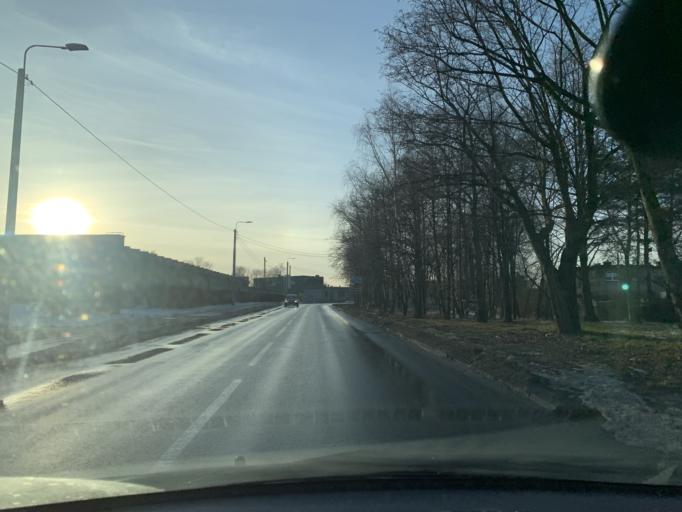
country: PL
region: Silesian Voivodeship
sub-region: Powiat tarnogorski
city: Radzionkow
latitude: 50.3850
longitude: 18.8948
